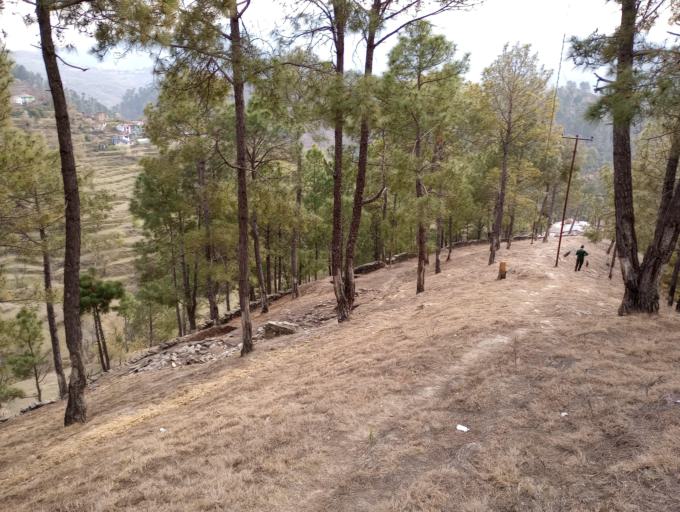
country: IN
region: Uttarakhand
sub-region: Almora
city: Almora
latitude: 29.6306
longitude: 79.5918
